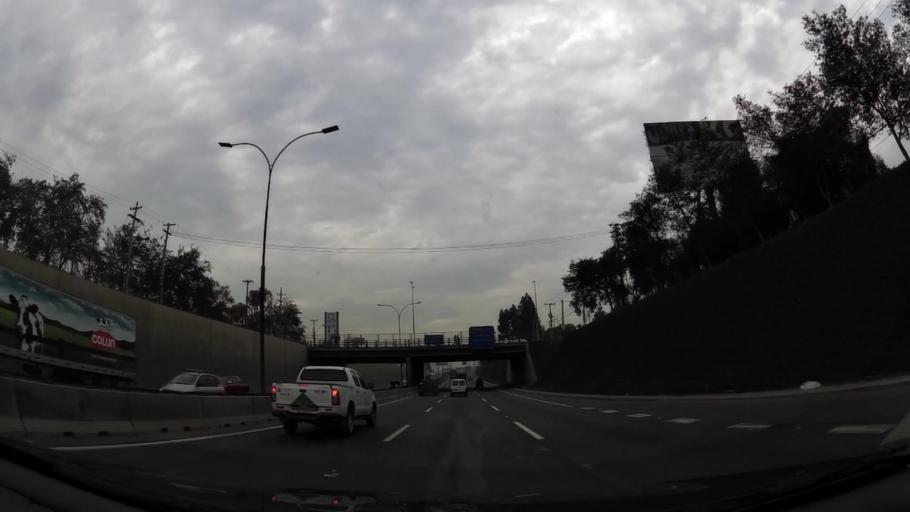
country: CL
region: Santiago Metropolitan
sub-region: Provincia de Santiago
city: Lo Prado
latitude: -33.3749
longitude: -70.6963
